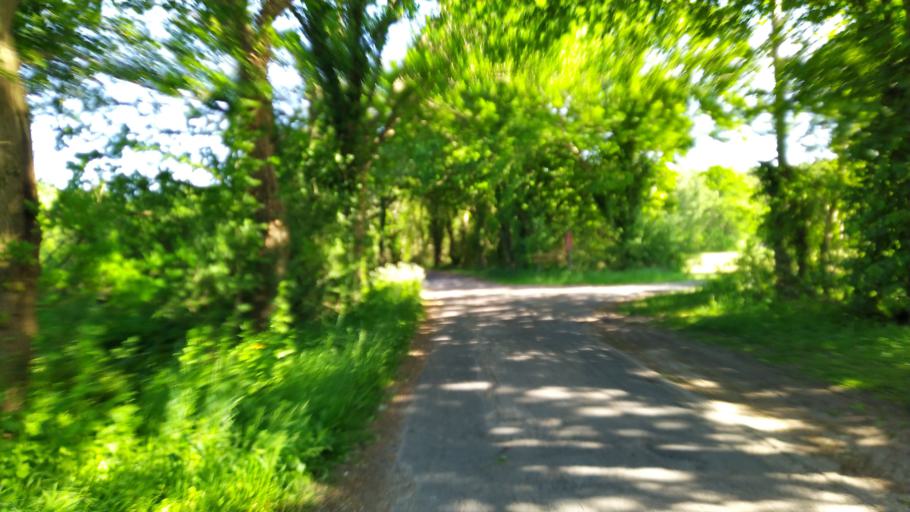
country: DE
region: Lower Saxony
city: Ahlerstedt
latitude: 53.4264
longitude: 9.4724
